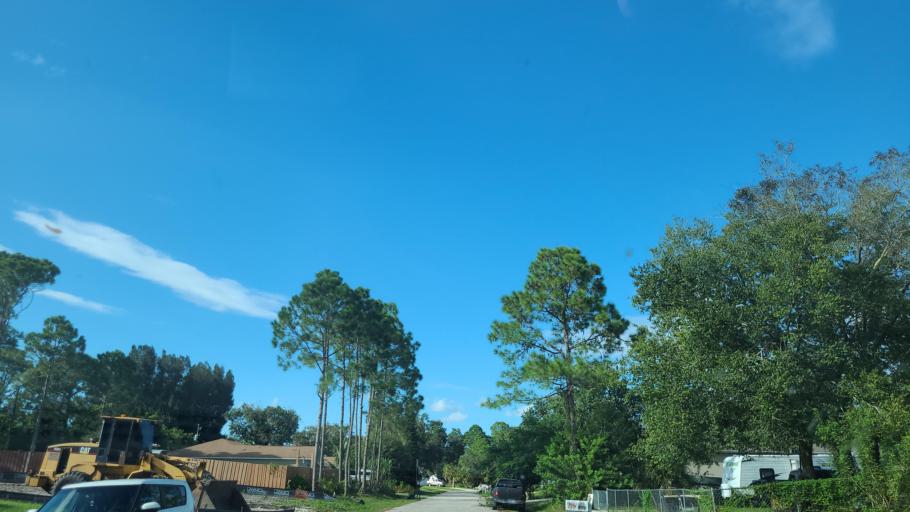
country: US
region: Florida
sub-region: Brevard County
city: June Park
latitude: 27.9822
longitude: -80.6710
